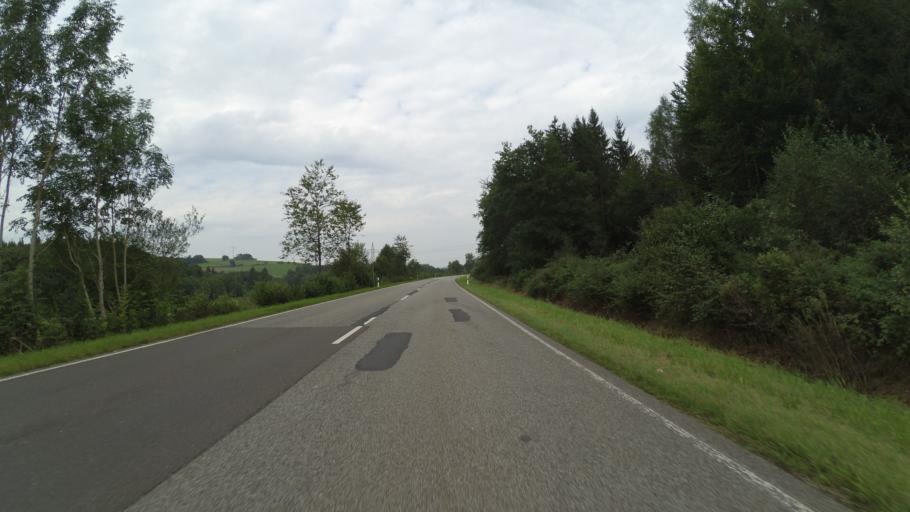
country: DE
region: Rheinland-Pfalz
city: Greimerath
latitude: 49.5760
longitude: 6.6661
